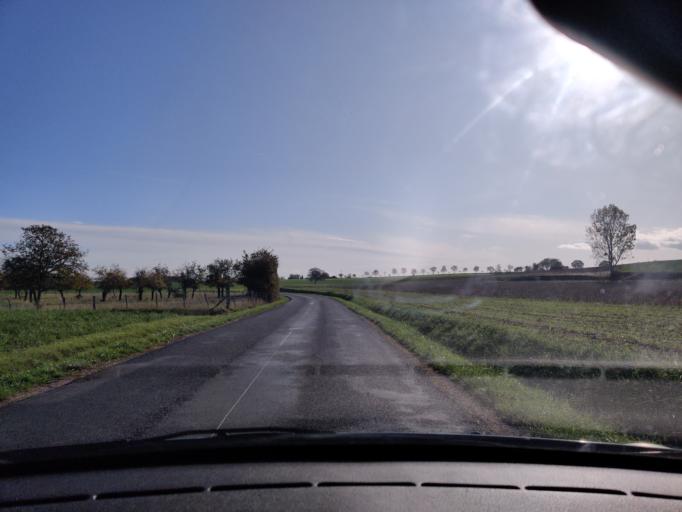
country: FR
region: Auvergne
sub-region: Departement du Puy-de-Dome
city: Aigueperse
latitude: 46.0360
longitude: 3.1545
